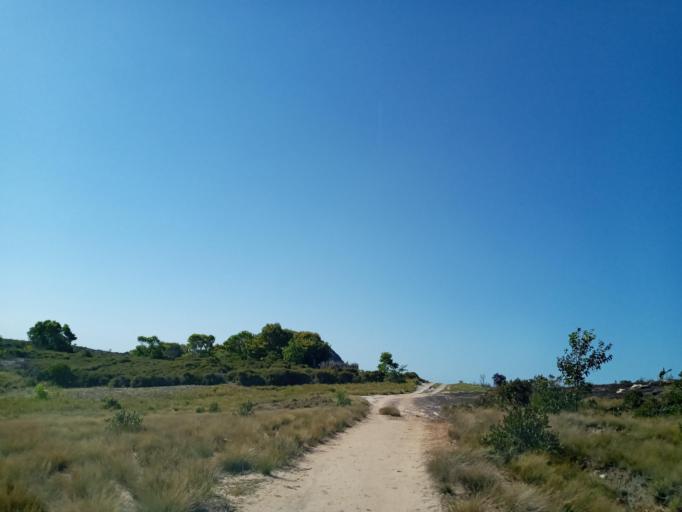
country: MG
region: Anosy
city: Fort Dauphin
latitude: -24.9073
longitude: 47.0913
